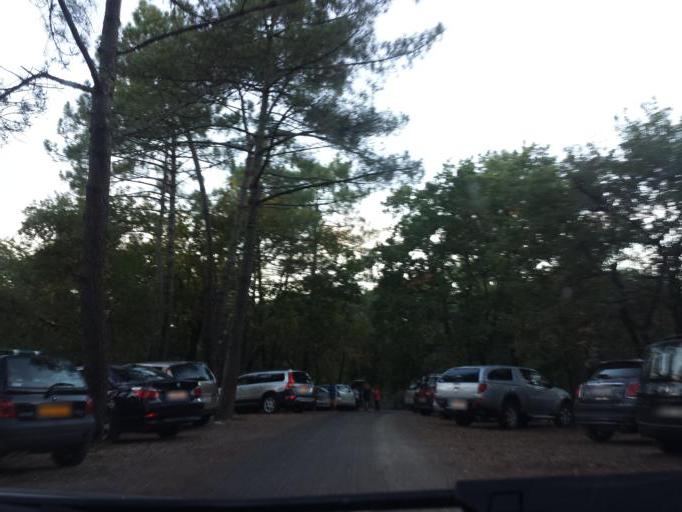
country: FR
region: Aquitaine
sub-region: Departement de la Gironde
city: Arcachon
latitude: 44.5979
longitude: -1.1993
